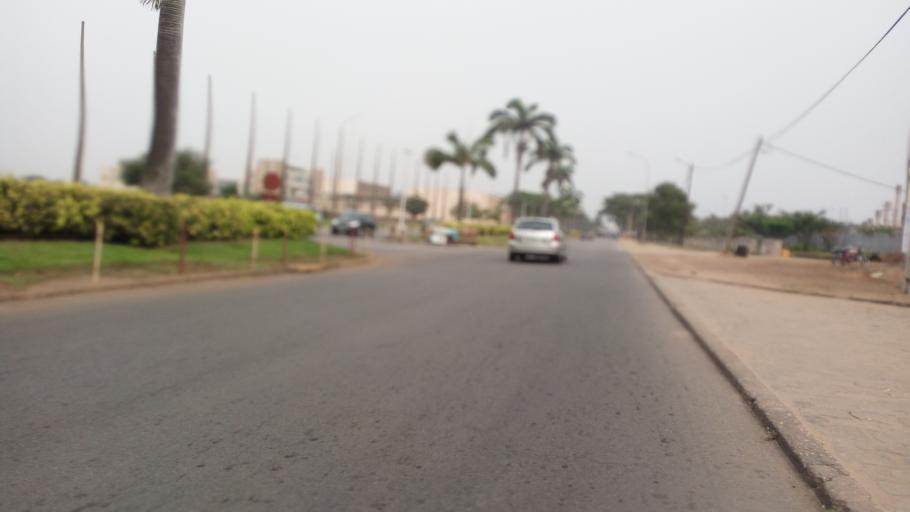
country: BJ
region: Littoral
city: Cotonou
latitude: 6.3487
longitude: 2.4013
